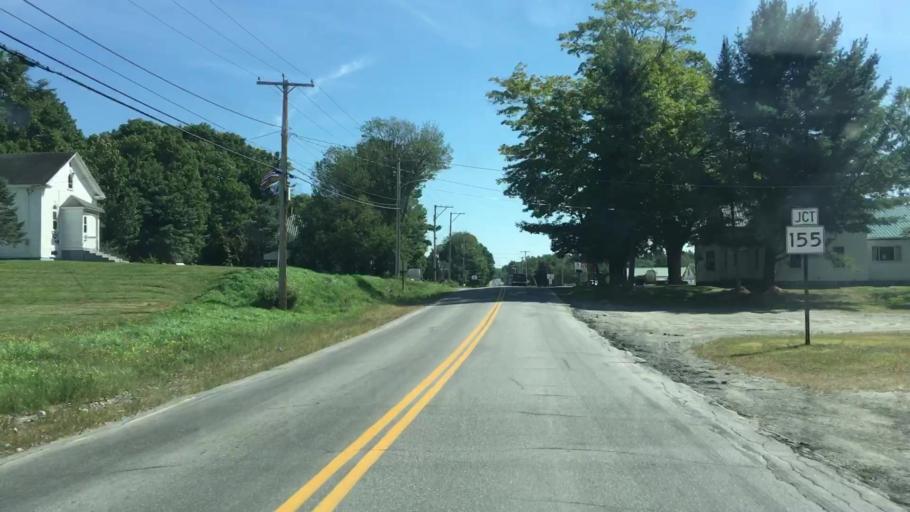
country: US
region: Maine
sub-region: Penobscot County
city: Bradford
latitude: 45.1680
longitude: -68.8460
